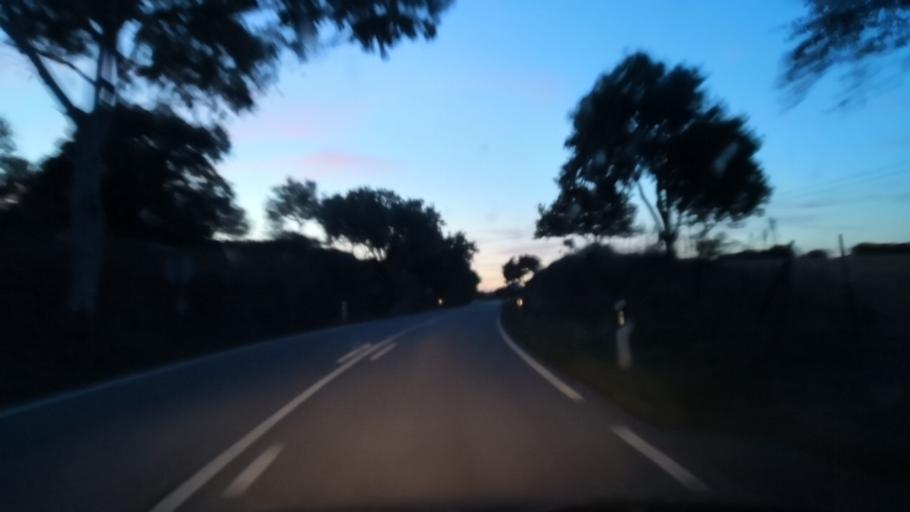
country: ES
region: Extremadura
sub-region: Provincia de Caceres
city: Piedras Albas
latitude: 39.8433
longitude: -6.9784
